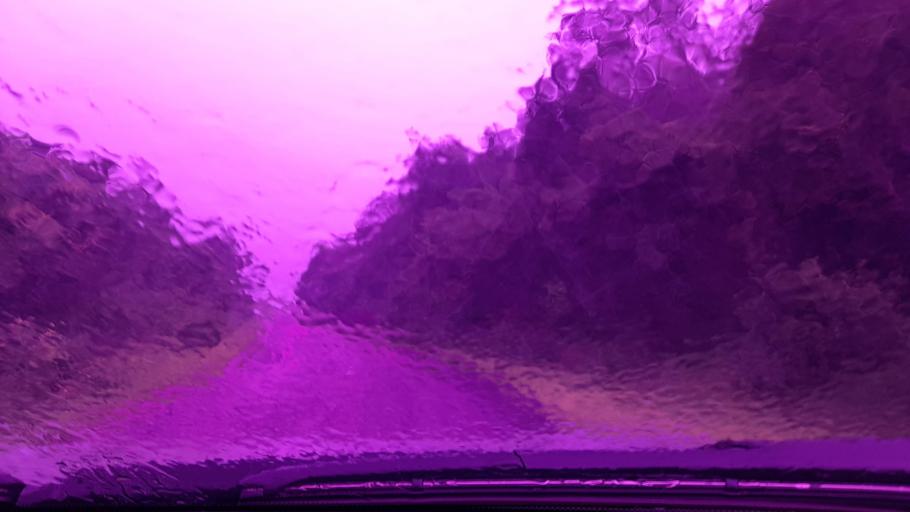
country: ET
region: Oromiya
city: Metu
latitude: 8.4686
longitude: 35.6397
